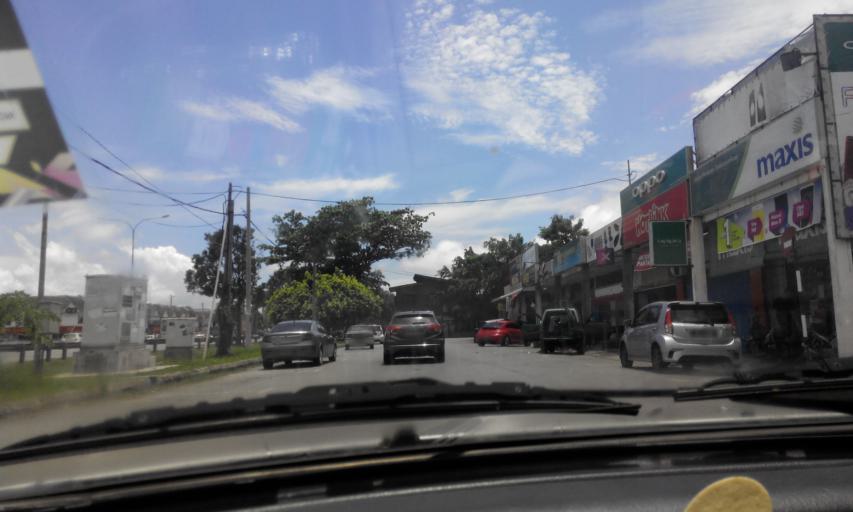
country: MY
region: Perak
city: Parit Buntar
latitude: 5.1208
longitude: 100.4862
